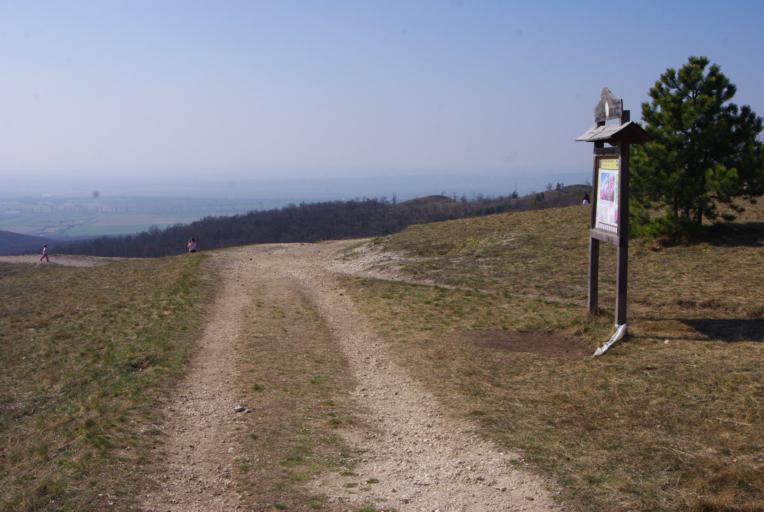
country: HU
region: Pest
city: Telki
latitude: 47.5419
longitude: 18.8695
